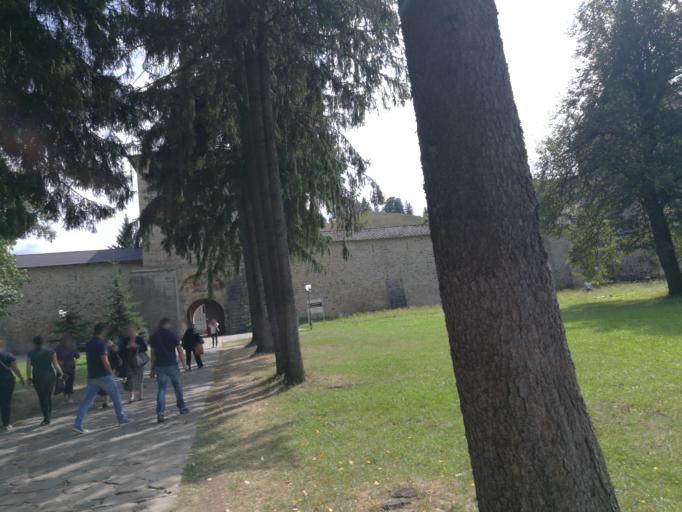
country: RO
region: Suceava
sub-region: Comuna Sucevita
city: Sucevita
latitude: 47.7789
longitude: 25.7106
